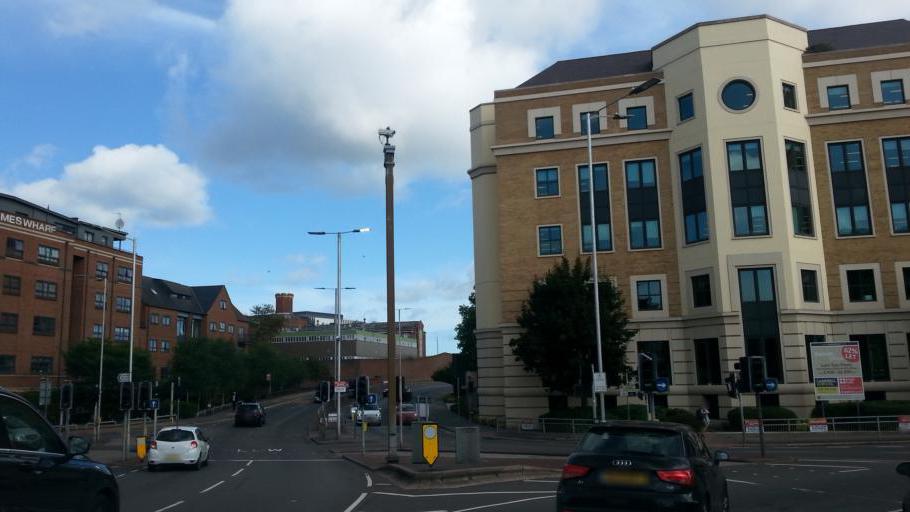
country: GB
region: England
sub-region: Reading
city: Reading
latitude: 51.4546
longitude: -0.9622
